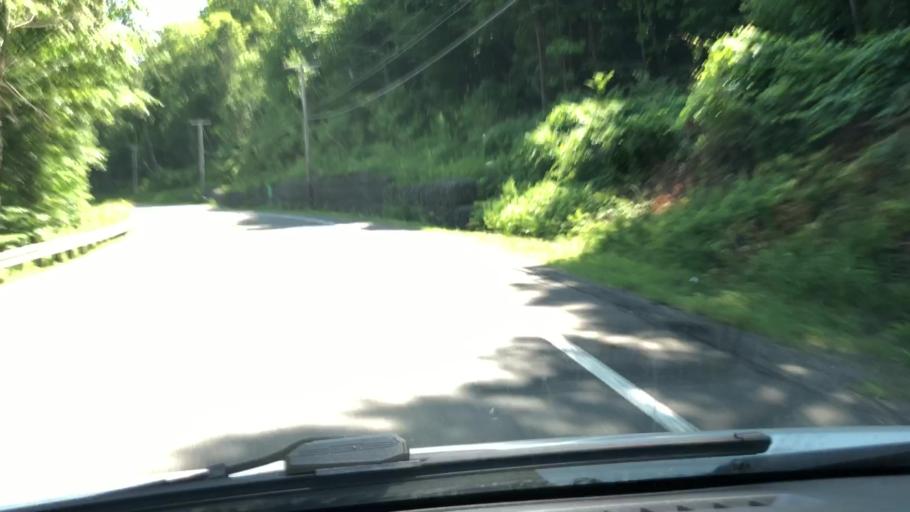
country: US
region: Massachusetts
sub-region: Hampshire County
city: Williamsburg
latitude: 42.4101
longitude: -72.7587
